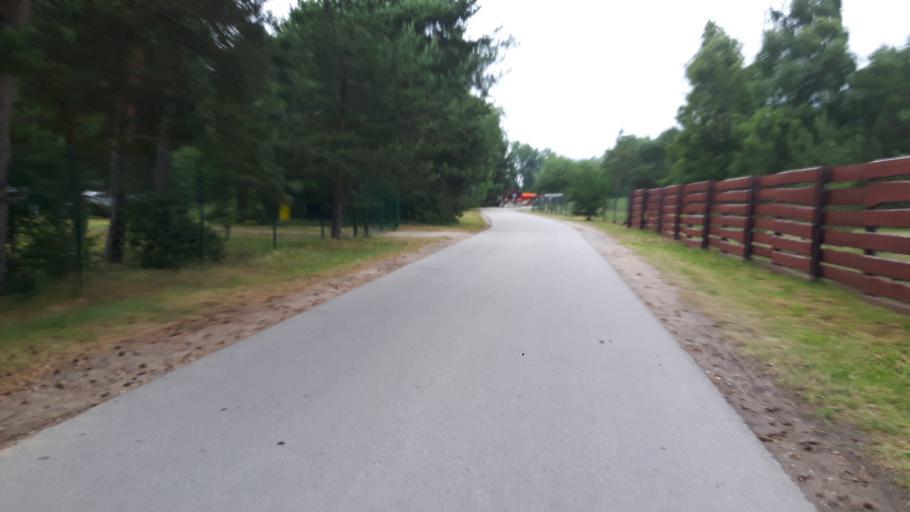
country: LT
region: Klaipedos apskritis
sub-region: Palanga
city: Sventoji
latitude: 56.0130
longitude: 21.0760
